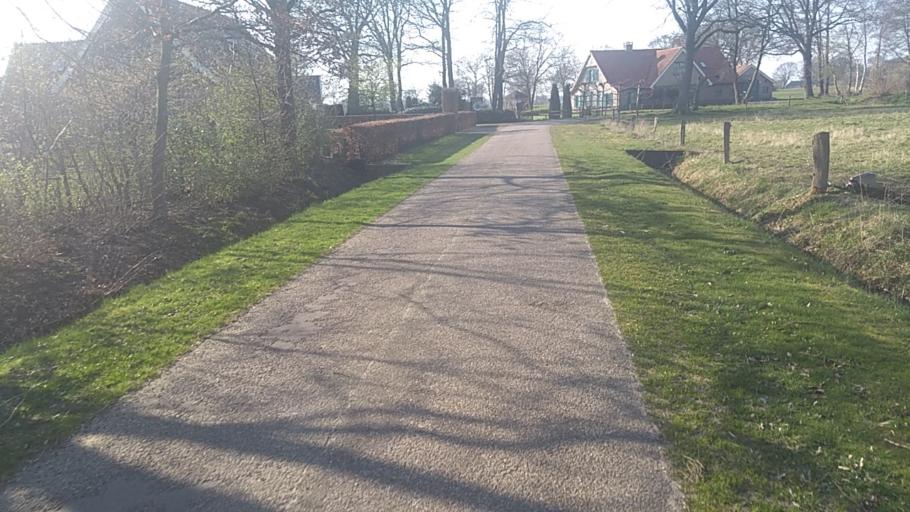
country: NL
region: Overijssel
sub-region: Gemeente Almelo
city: Almelo
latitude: 52.3899
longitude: 6.7160
